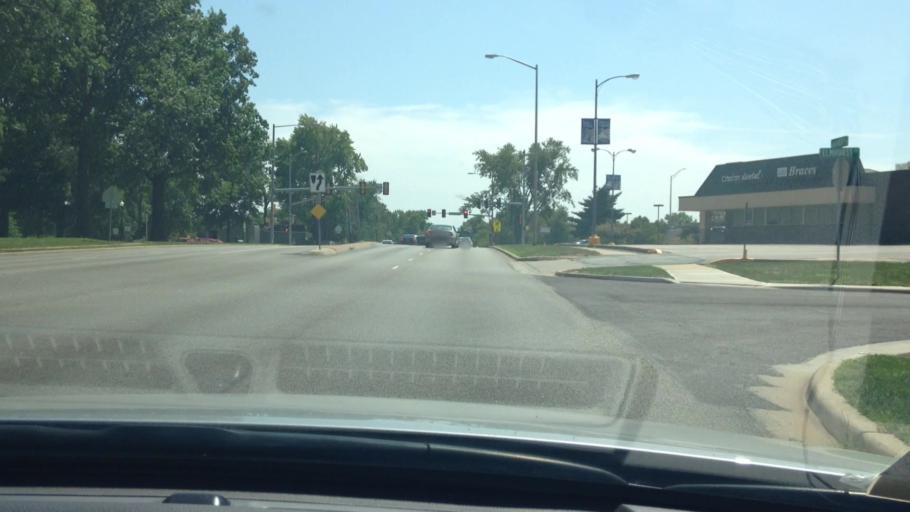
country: US
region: Kansas
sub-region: Johnson County
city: Overland Park
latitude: 38.9742
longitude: -94.6864
